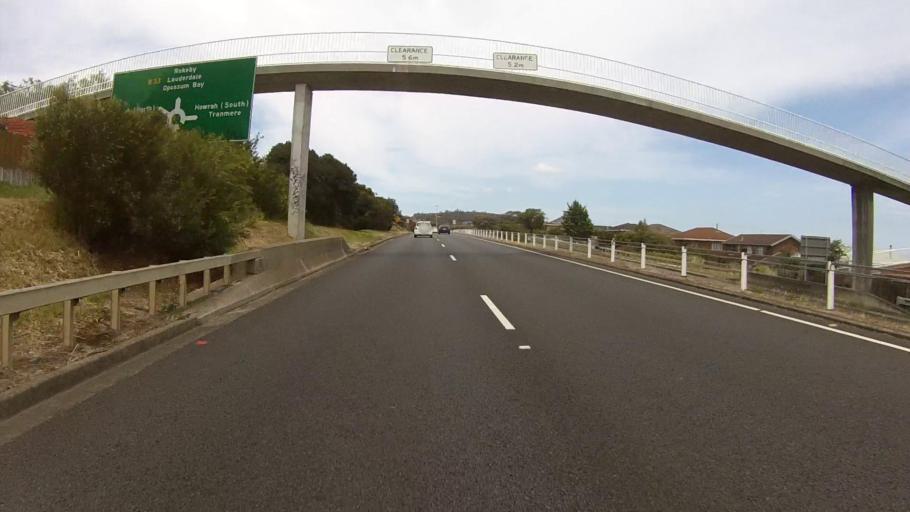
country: AU
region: Tasmania
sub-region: Clarence
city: Howrah
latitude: -42.8757
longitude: 147.4040
